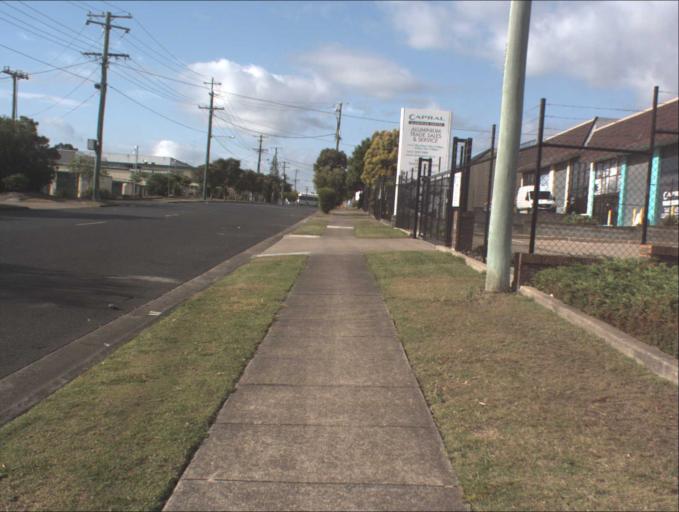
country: AU
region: Queensland
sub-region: Logan
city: Springwood
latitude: -27.6171
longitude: 153.1187
